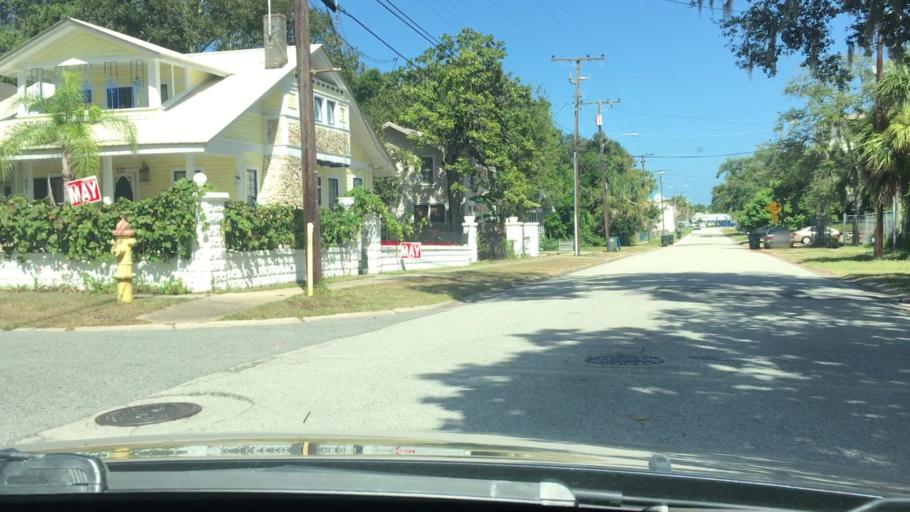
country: US
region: Florida
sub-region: Volusia County
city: Daytona Beach
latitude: 29.2213
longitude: -81.0265
